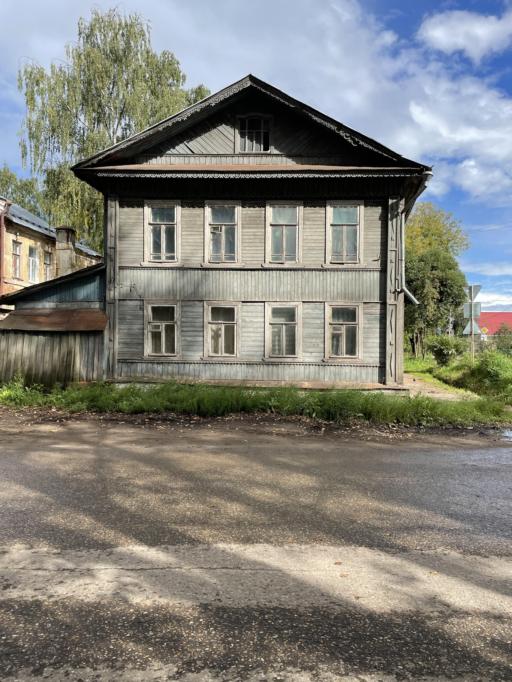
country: RU
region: Tverskaya
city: Vyshniy Volochek
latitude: 57.5802
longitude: 34.5585
